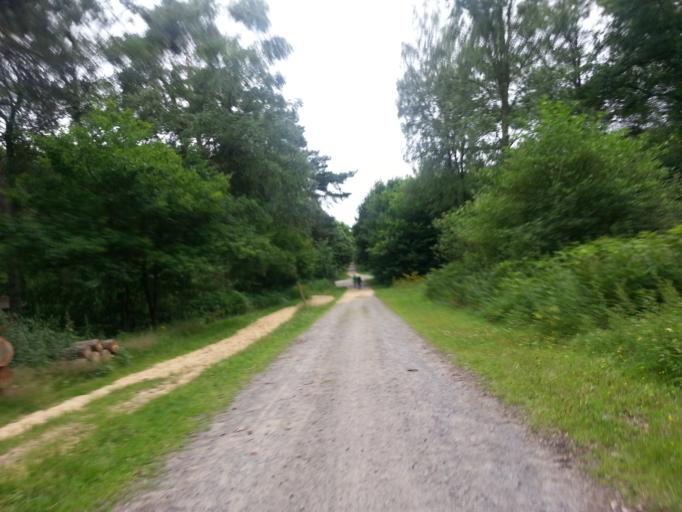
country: DE
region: North Rhine-Westphalia
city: Oer-Erkenschwick
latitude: 51.6807
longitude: 7.2235
